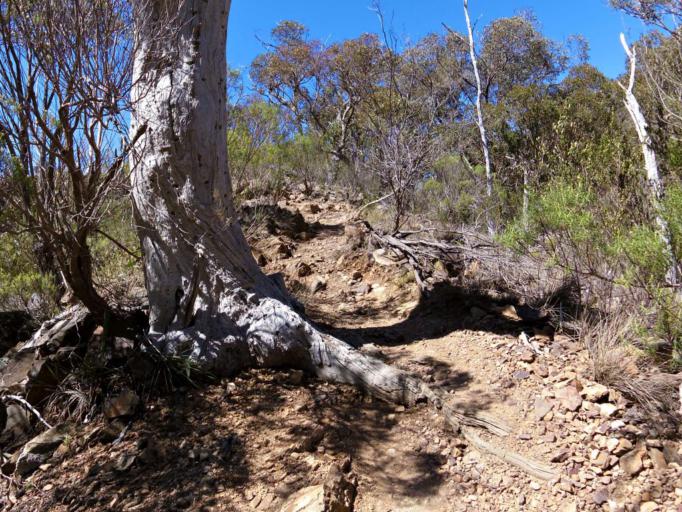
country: AU
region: Victoria
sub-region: Moorabool
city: Bacchus Marsh
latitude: -37.6566
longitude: 144.3462
